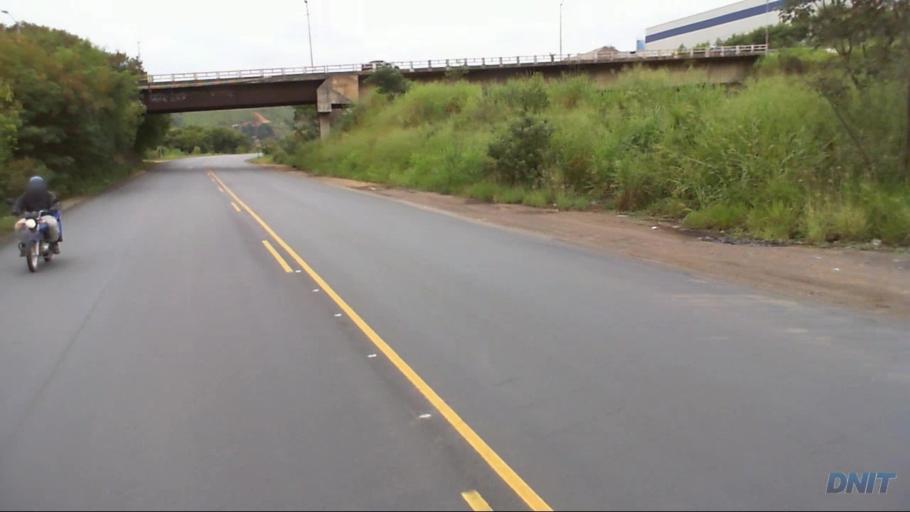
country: BR
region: Minas Gerais
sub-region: Coronel Fabriciano
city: Coronel Fabriciano
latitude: -19.5254
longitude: -42.6409
